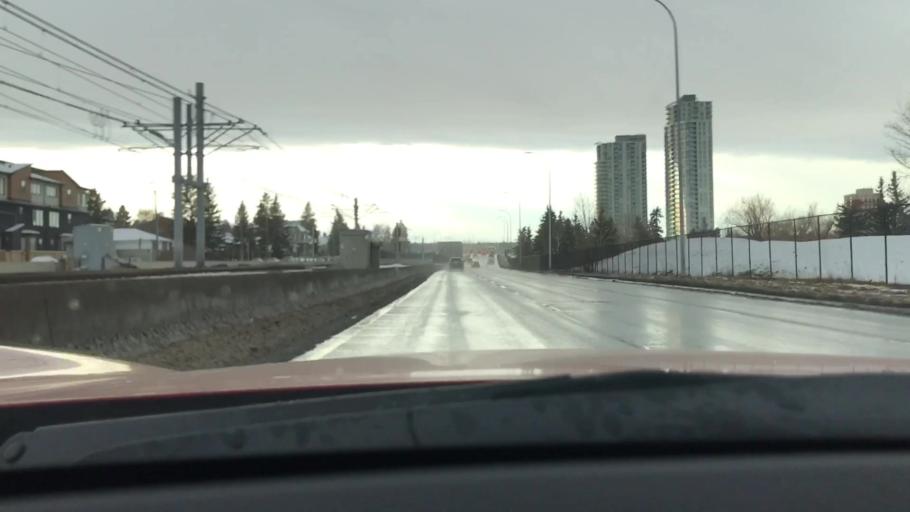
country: CA
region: Alberta
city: Calgary
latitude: 51.0418
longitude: -114.1279
